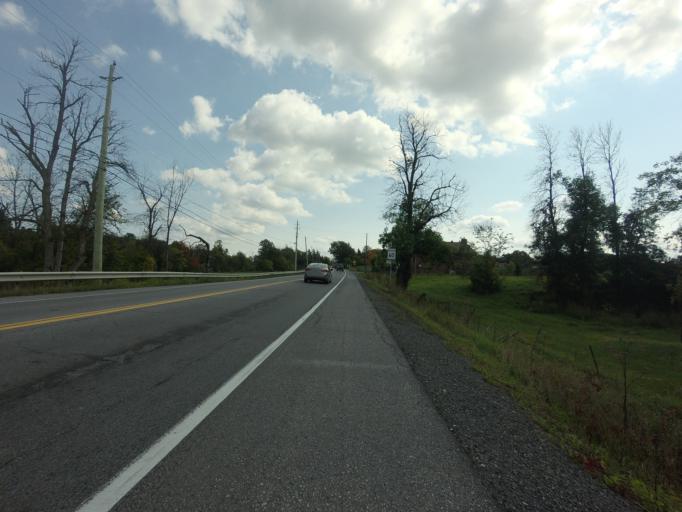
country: CA
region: Ontario
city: Bells Corners
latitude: 45.2304
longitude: -75.6925
